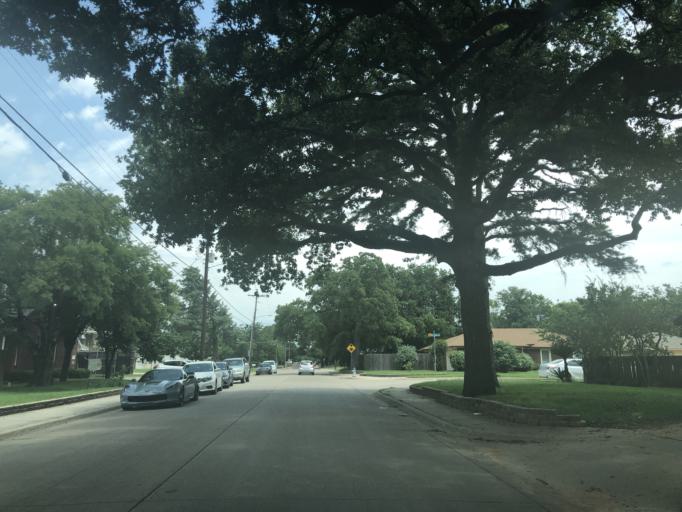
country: US
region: Texas
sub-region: Dallas County
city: Irving
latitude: 32.7957
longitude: -96.9300
